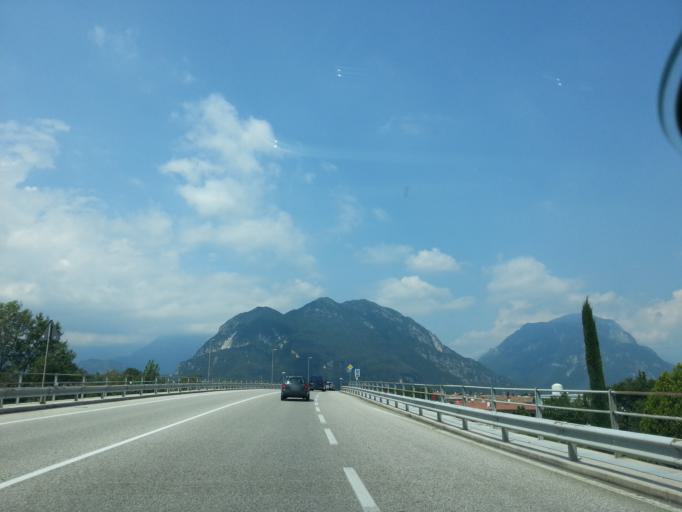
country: IT
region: Friuli Venezia Giulia
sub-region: Provincia di Udine
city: Gemona
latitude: 46.2587
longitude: 13.1092
